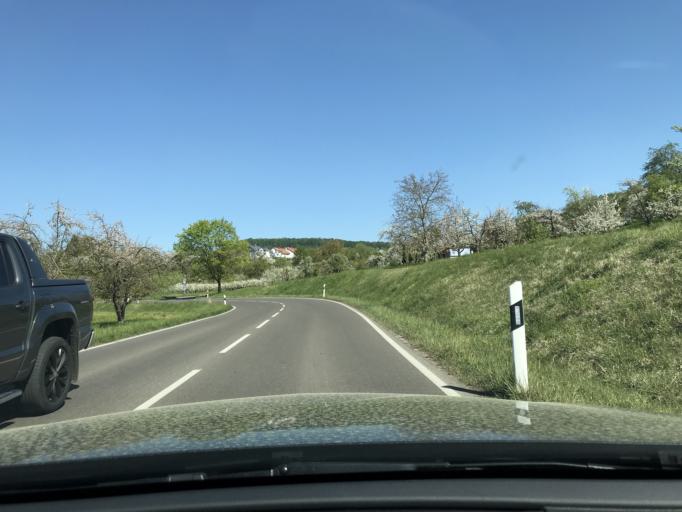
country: DE
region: Baden-Wuerttemberg
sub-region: Regierungsbezirk Stuttgart
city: Korb
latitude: 48.8332
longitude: 9.3708
